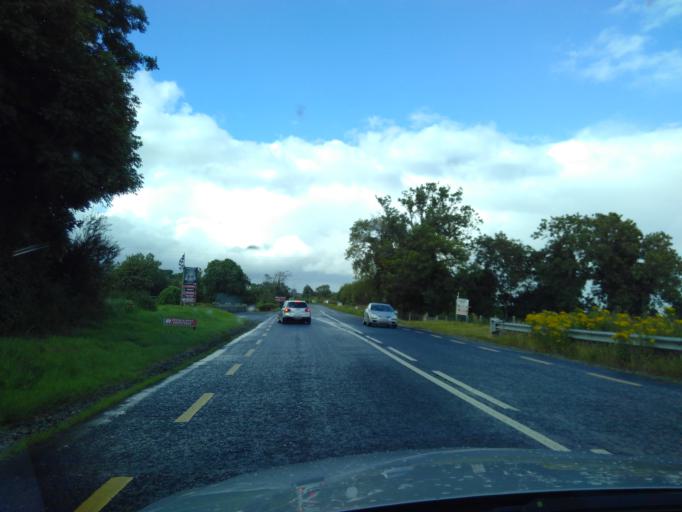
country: IE
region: Ulster
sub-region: County Donegal
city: Ramelton
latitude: 54.9834
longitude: -7.6728
